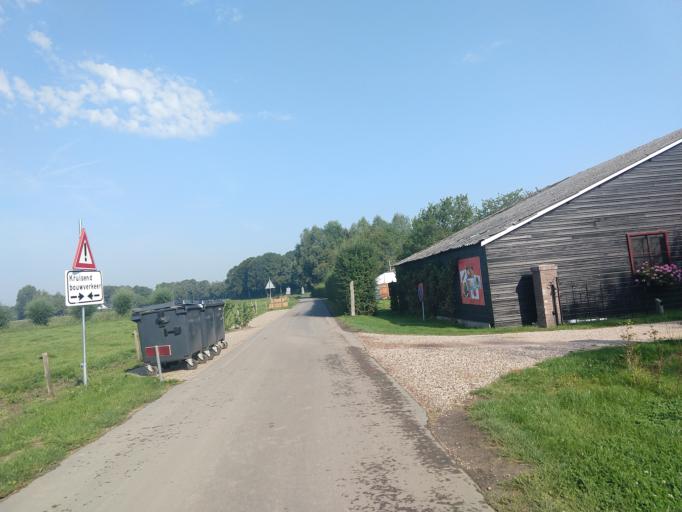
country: NL
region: Gelderland
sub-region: Gemeente Lochem
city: Eefde
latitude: 52.1633
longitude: 6.2484
